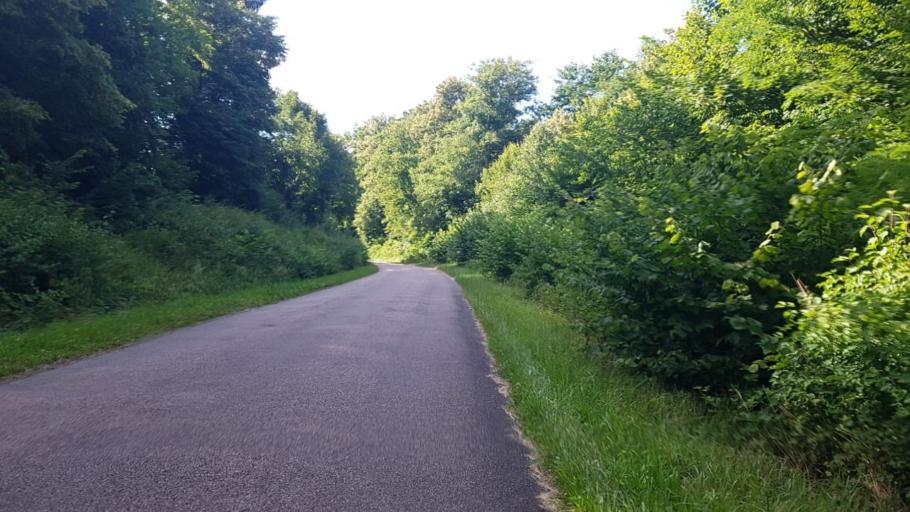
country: FR
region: Picardie
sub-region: Departement de l'Oise
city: Senlis
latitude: 49.1831
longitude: 2.6138
